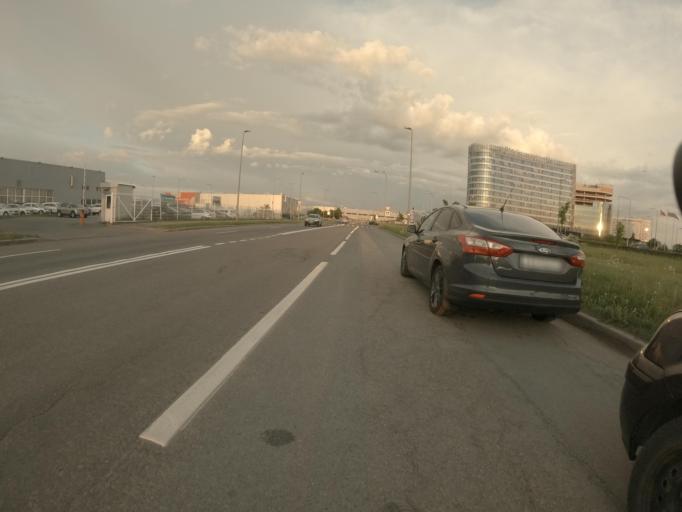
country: RU
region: St.-Petersburg
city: Kupchino
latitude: 59.8101
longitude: 30.3162
